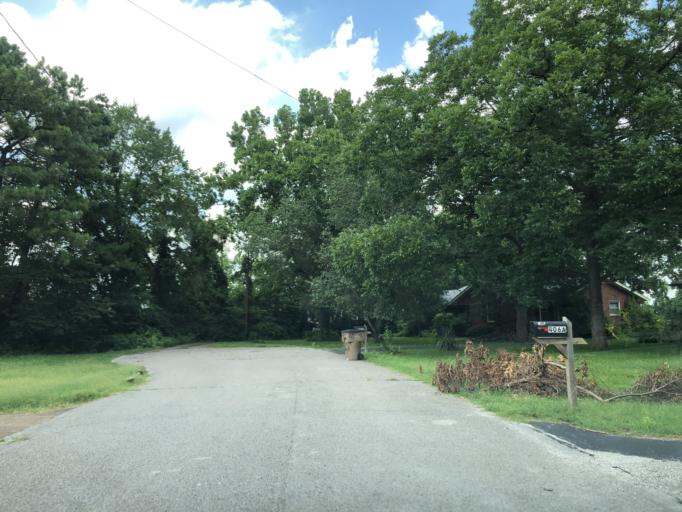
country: US
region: Tennessee
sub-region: Davidson County
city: Nashville
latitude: 36.1304
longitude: -86.7223
